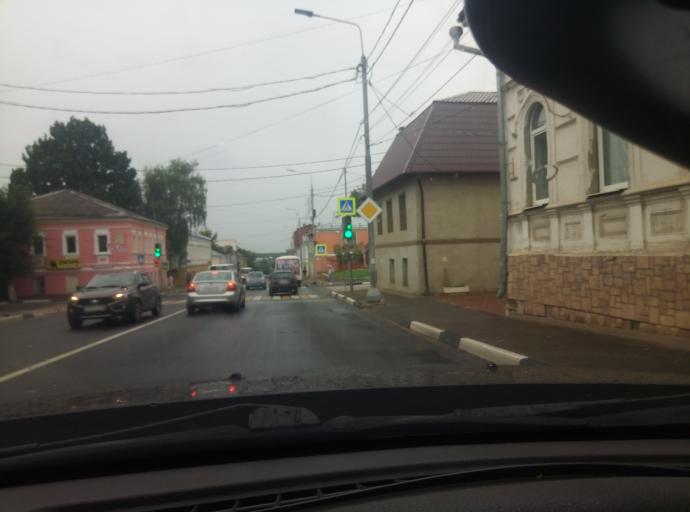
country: RU
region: Moskovskaya
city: Serpukhov
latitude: 54.9158
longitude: 37.4178
